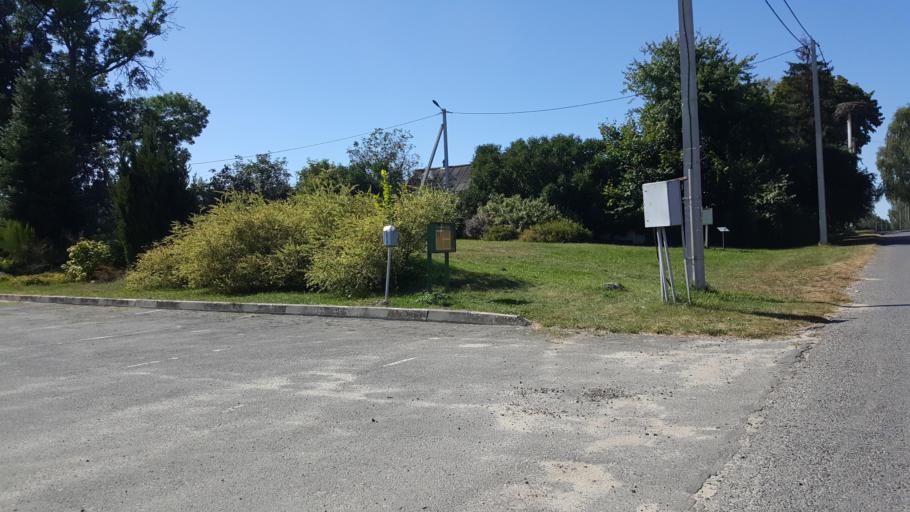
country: BY
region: Brest
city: Vysokaye
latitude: 52.2212
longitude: 23.4208
